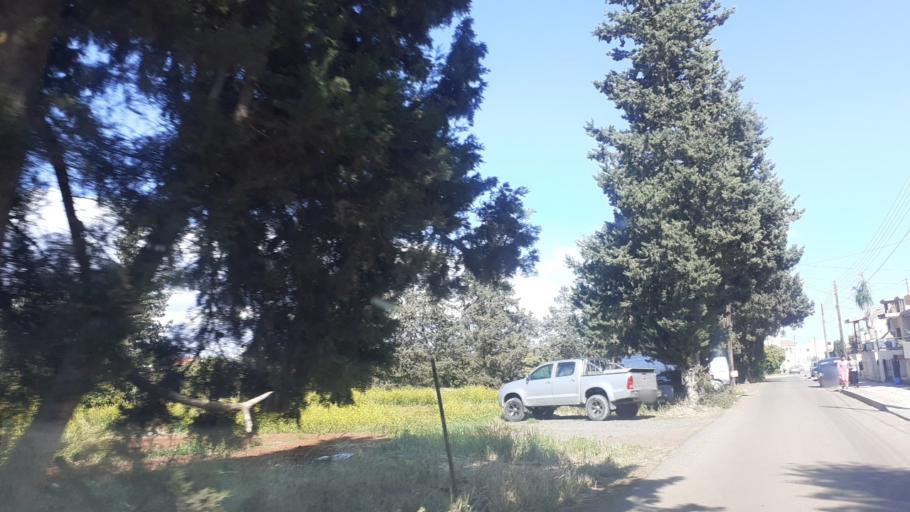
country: CY
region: Limassol
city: Limassol
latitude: 34.6616
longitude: 32.9996
